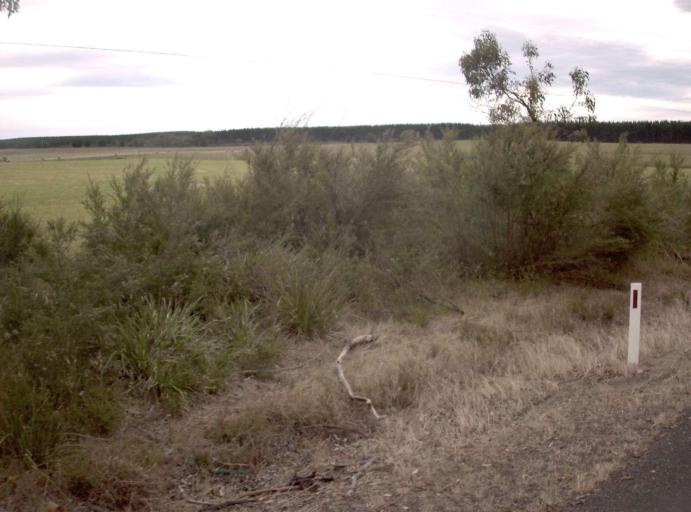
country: AU
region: Victoria
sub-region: Wellington
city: Sale
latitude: -38.2266
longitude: 147.0555
